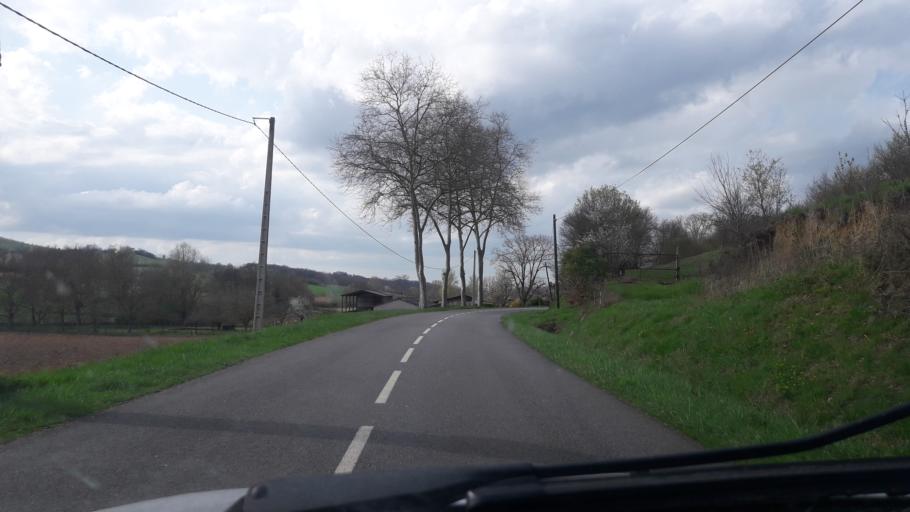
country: FR
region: Midi-Pyrenees
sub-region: Departement de la Haute-Garonne
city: Montesquieu-Volvestre
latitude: 43.2379
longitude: 1.2709
